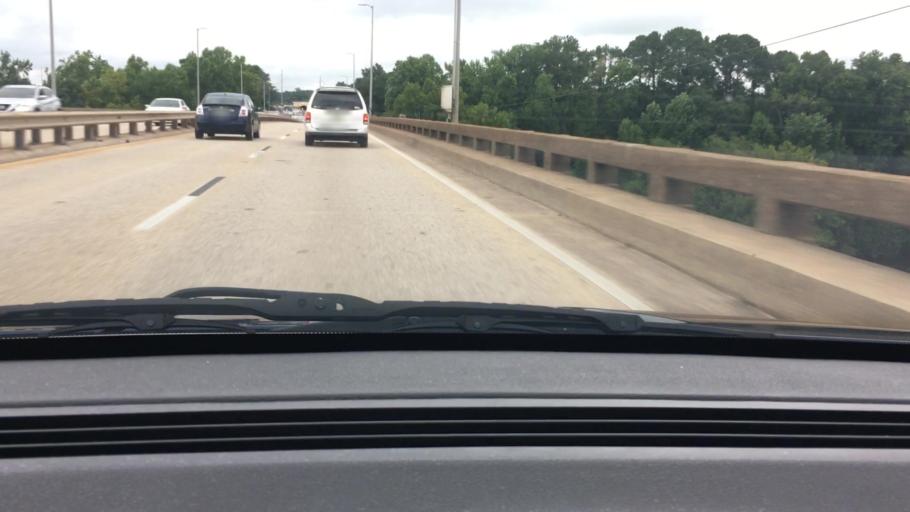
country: US
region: Alabama
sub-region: Tuscaloosa County
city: Tuscaloosa
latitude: 33.2226
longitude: -87.5320
